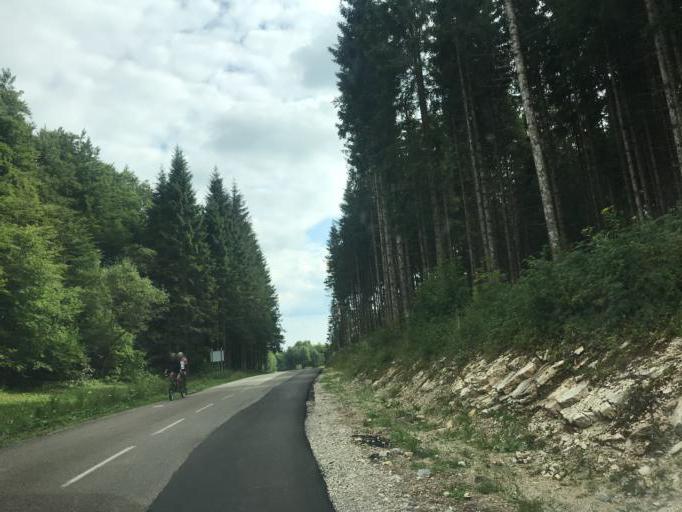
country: FR
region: Franche-Comte
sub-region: Departement du Jura
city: Valfin-les-Saint-Claude
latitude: 46.4769
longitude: 5.8374
